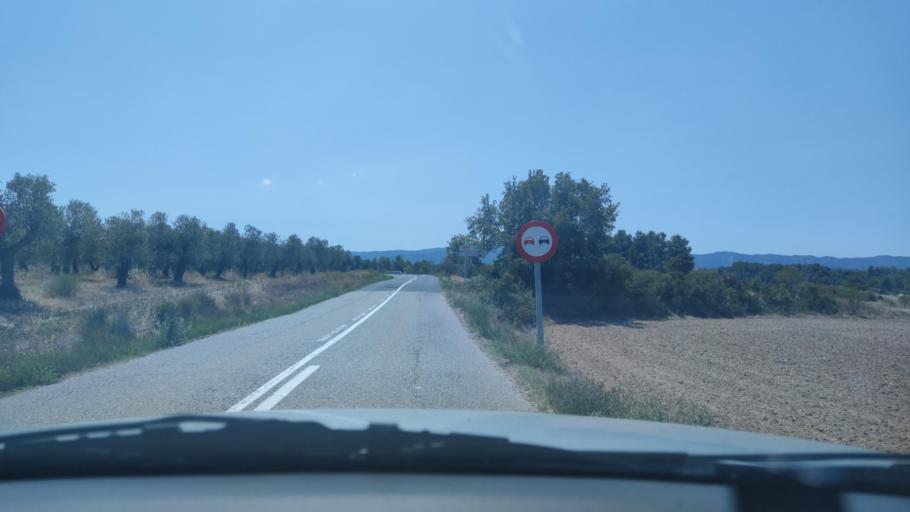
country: ES
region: Catalonia
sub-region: Provincia de Lleida
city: Vinaixa
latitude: 41.4185
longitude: 0.9547
